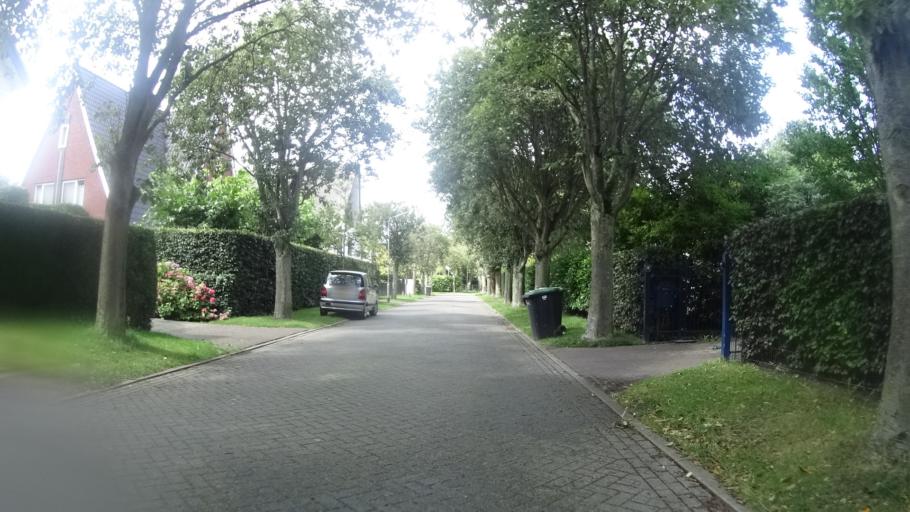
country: NL
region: North Holland
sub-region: Gemeente Alkmaar
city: Alkmaar
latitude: 52.6753
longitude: 4.6973
